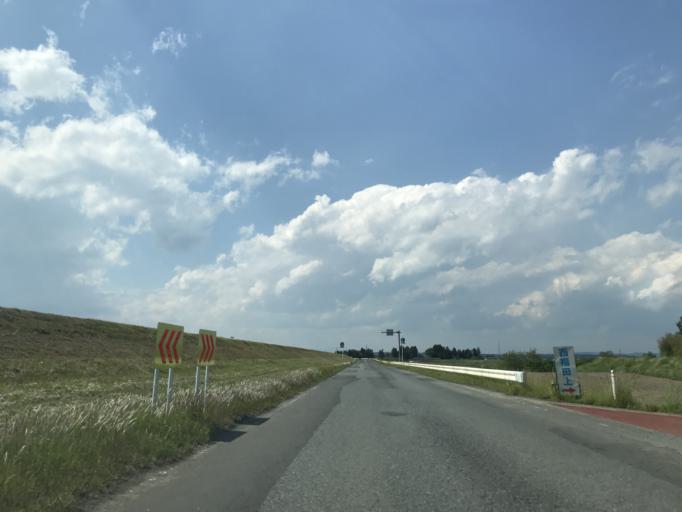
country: JP
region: Miyagi
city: Matsushima
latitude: 38.4388
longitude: 141.1174
